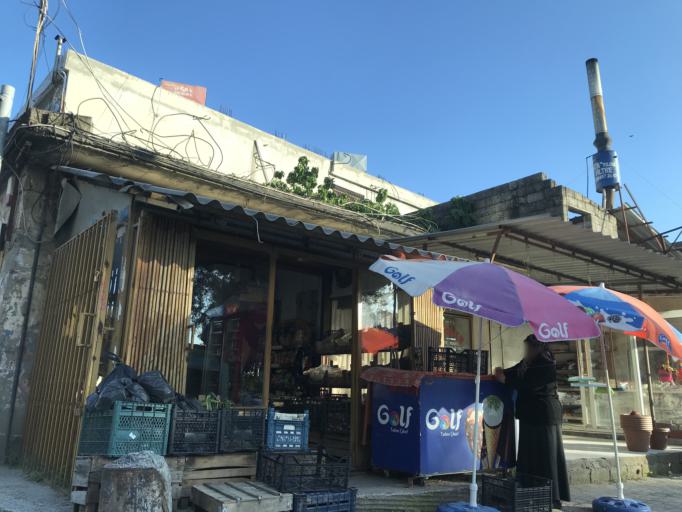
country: TR
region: Hatay
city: Samandag
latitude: 36.0827
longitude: 35.9962
